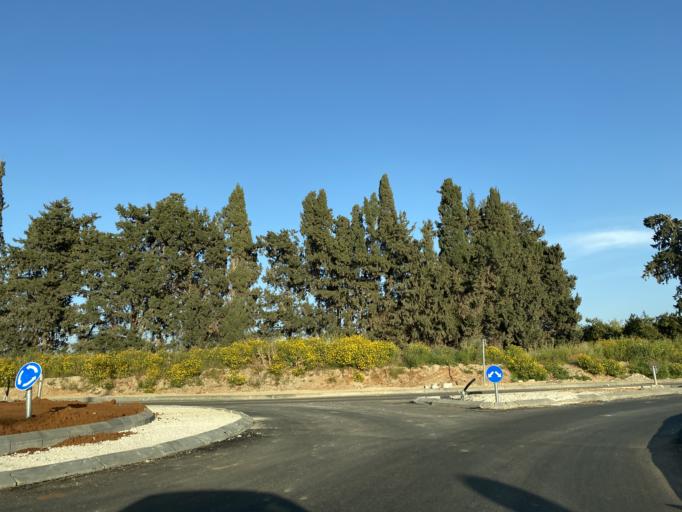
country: IL
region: Tel Aviv
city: Herzliyya
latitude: 32.1552
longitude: 34.8169
